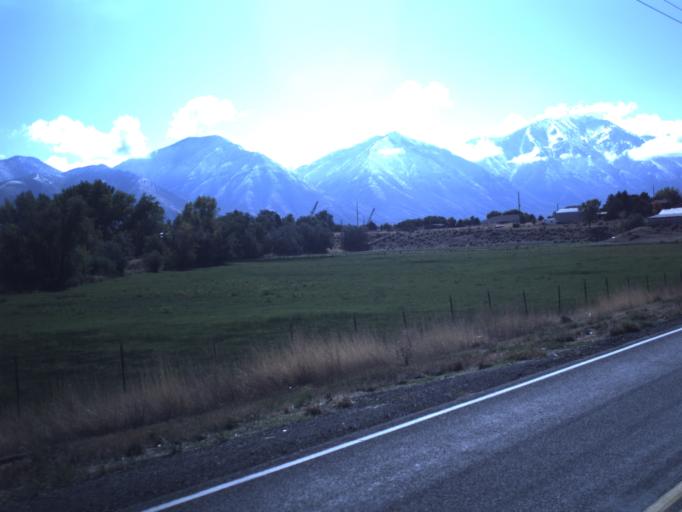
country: US
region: Utah
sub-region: Utah County
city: Spanish Fork
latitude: 40.1023
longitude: -111.6806
